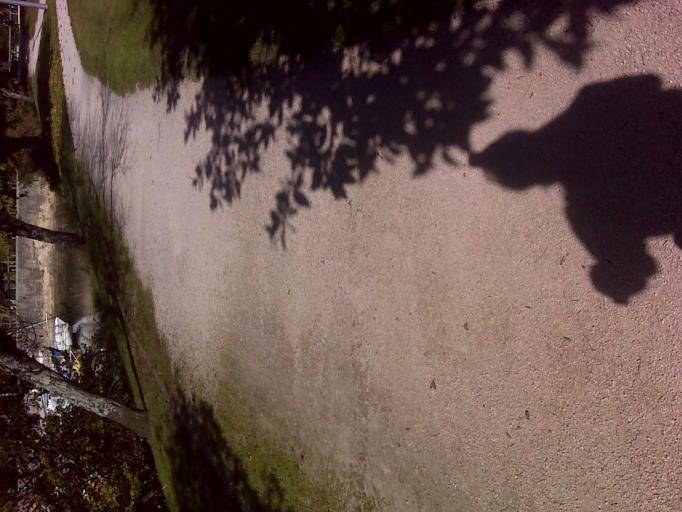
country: FR
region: Poitou-Charentes
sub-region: Departement de la Charente-Maritime
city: Marennes
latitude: 45.8192
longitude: -1.1107
